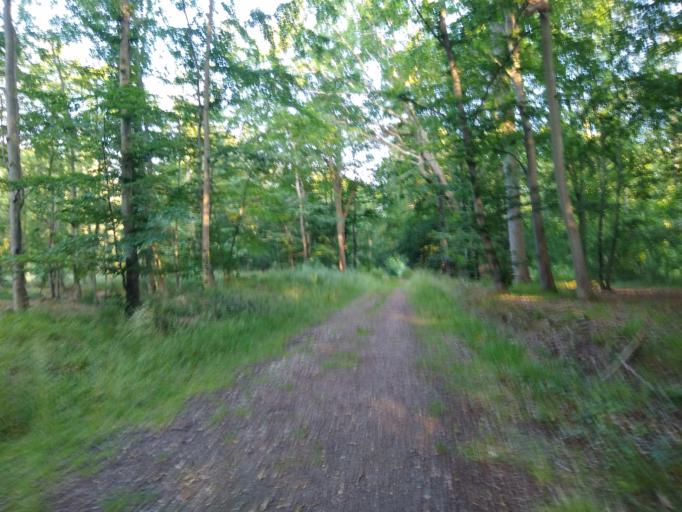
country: DK
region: South Denmark
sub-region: Fredericia Kommune
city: Fredericia
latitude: 55.6214
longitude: 9.8430
